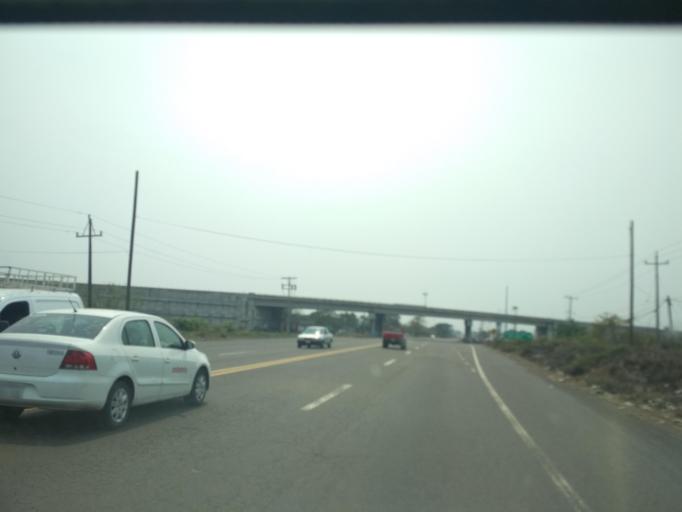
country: MX
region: Veracruz
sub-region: Veracruz
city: Delfino Victoria (Santa Fe)
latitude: 19.1882
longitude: -96.2730
